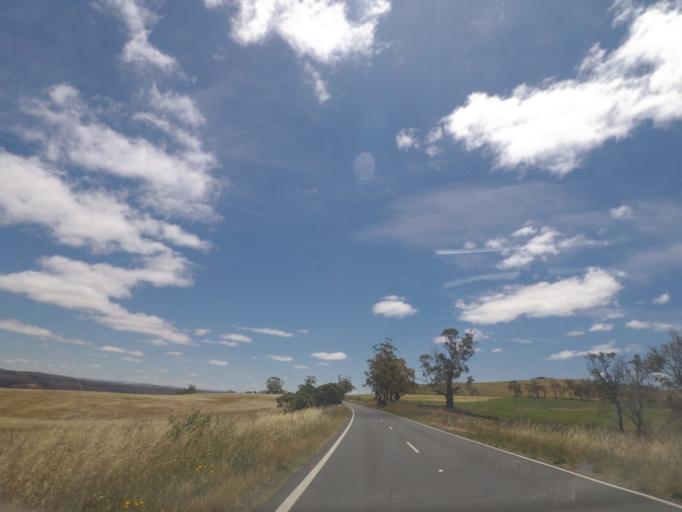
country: AU
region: Victoria
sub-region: Mount Alexander
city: Castlemaine
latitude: -37.2722
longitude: 144.1453
